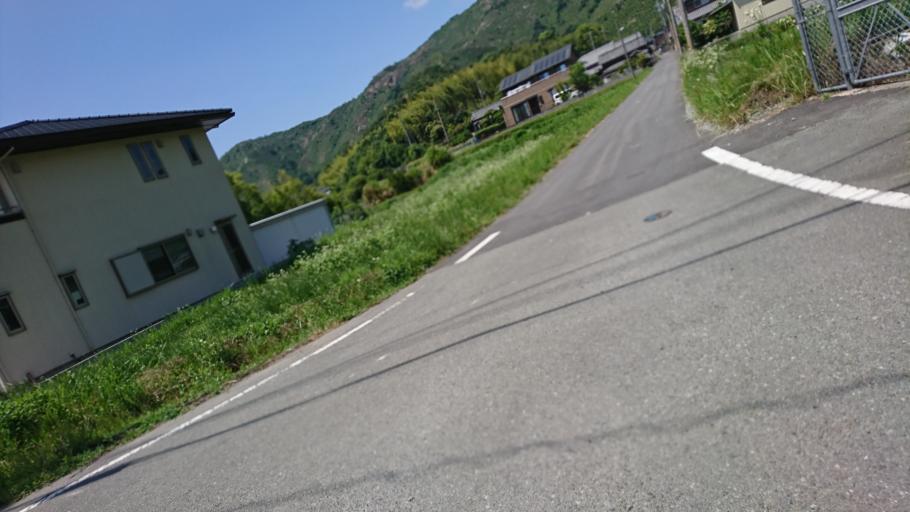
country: JP
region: Hyogo
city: Kakogawacho-honmachi
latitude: 34.8050
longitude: 134.7887
